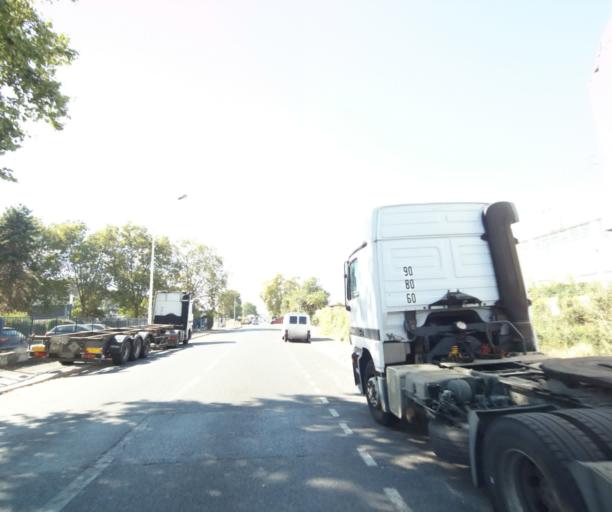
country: FR
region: Ile-de-France
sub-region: Departement des Hauts-de-Seine
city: Villeneuve-la-Garenne
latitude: 48.9249
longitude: 2.3184
